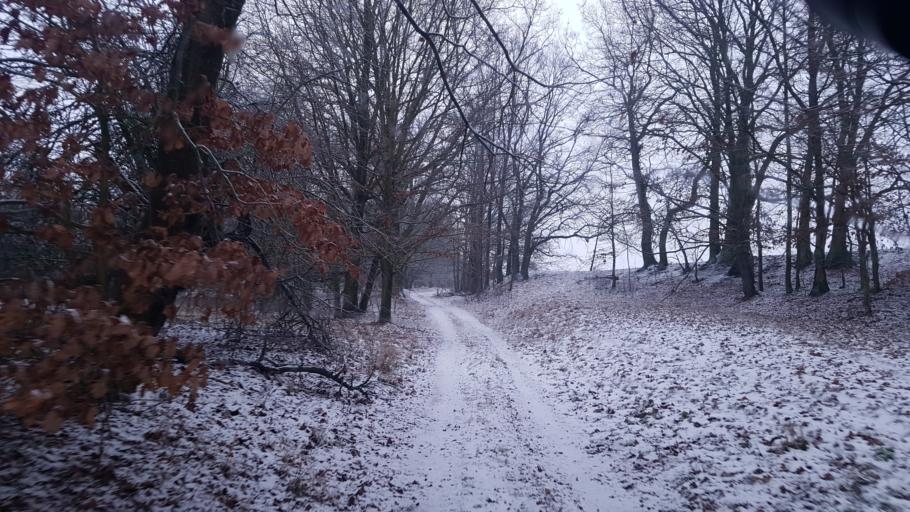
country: DE
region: Brandenburg
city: Schenkendobern
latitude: 51.9064
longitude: 14.5797
